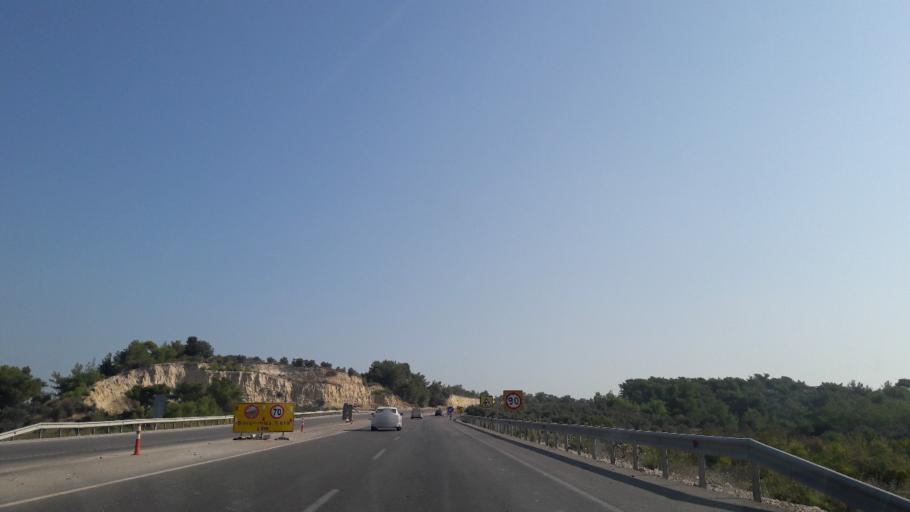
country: TR
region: Adana
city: Yuregir
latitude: 37.0783
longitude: 35.4729
